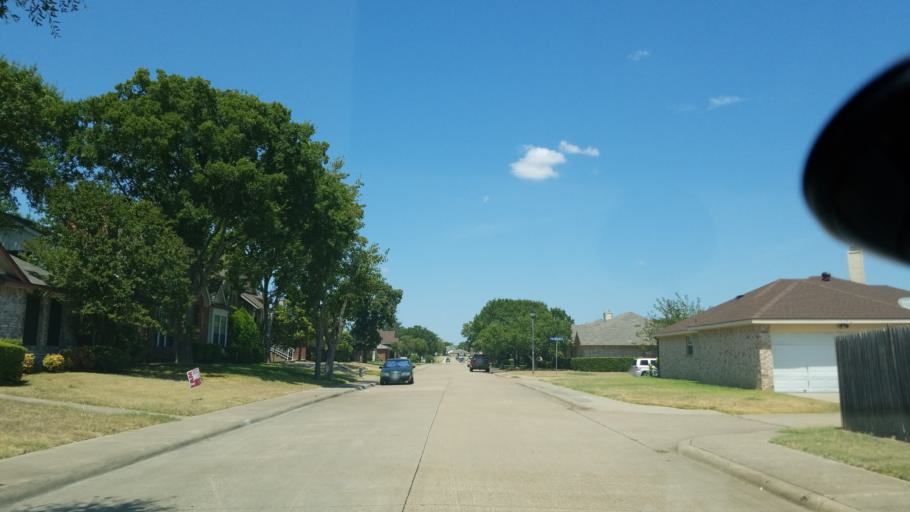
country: US
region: Texas
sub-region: Dallas County
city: Duncanville
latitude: 32.6376
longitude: -96.8858
